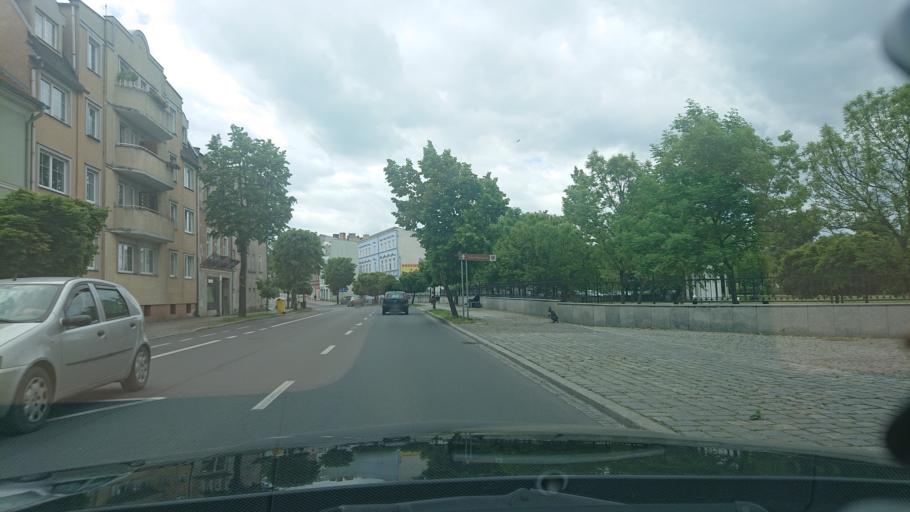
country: PL
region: Greater Poland Voivodeship
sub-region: Powiat gnieznienski
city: Gniezno
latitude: 52.5369
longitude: 17.5902
